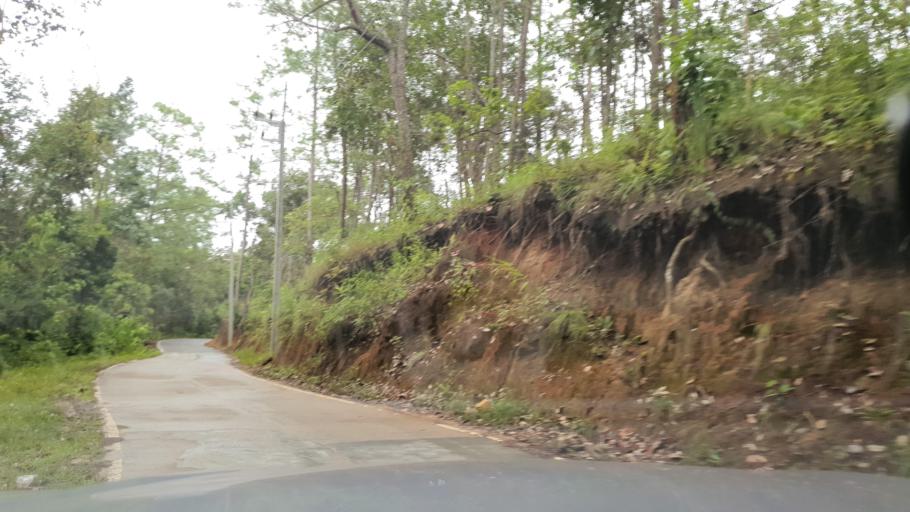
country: TH
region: Chiang Mai
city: Mae Wang
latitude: 18.6976
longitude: 98.5696
